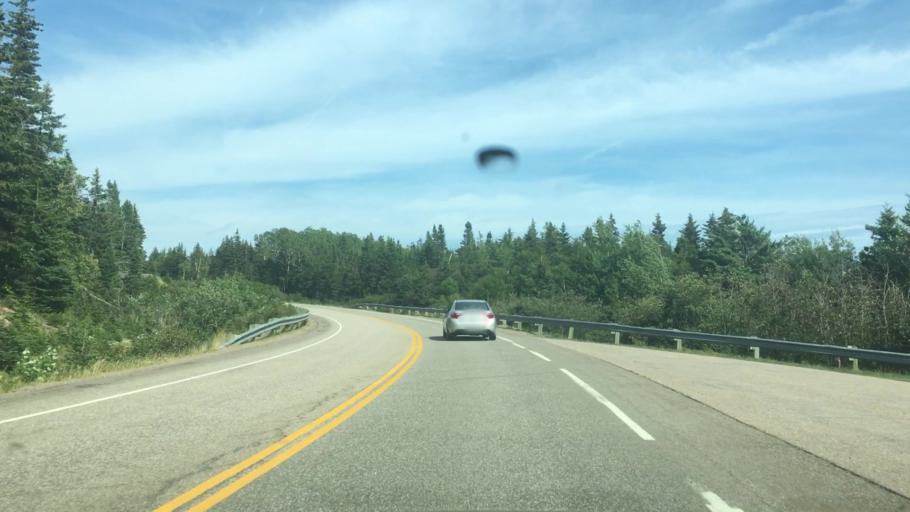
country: CA
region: Nova Scotia
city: Sydney Mines
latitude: 46.7138
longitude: -60.3558
